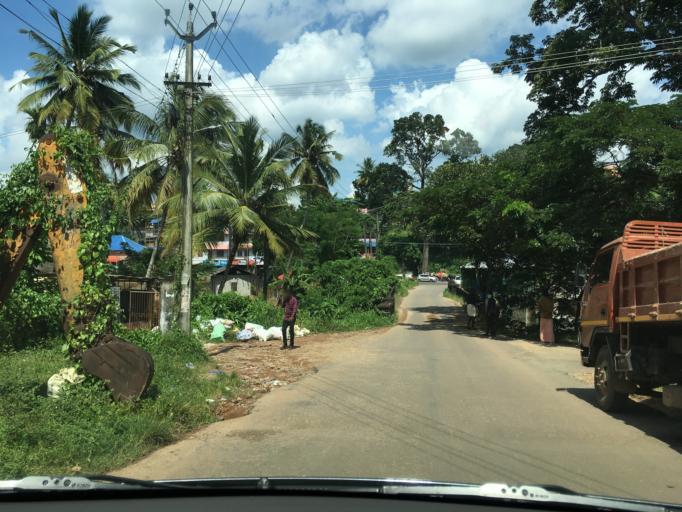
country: IN
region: Kerala
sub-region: Thiruvananthapuram
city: Nedumangad
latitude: 8.6088
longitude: 76.9974
